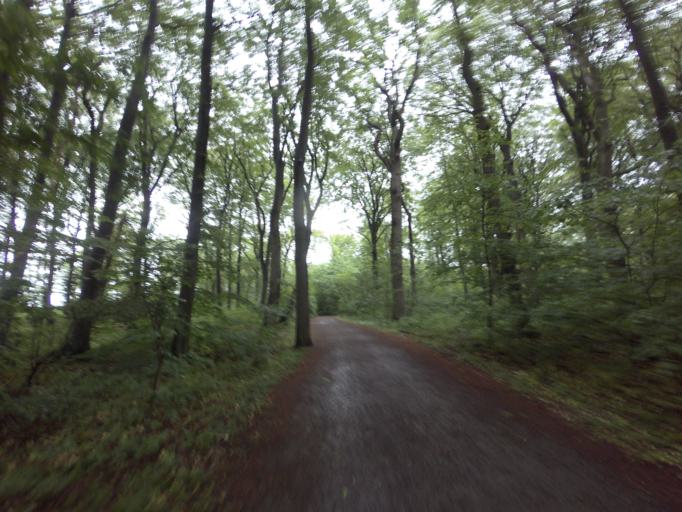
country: SE
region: Skane
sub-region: Helsingborg
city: Odakra
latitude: 56.0899
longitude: 12.7301
